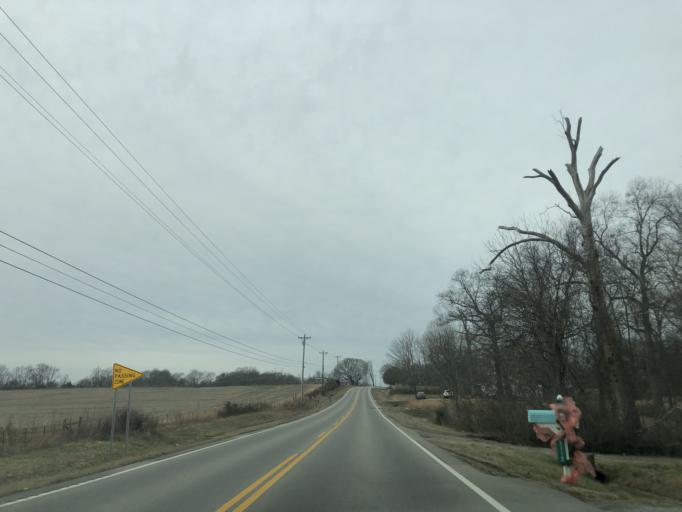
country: US
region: Tennessee
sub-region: Robertson County
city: Ridgetop
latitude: 36.3982
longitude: -86.8014
